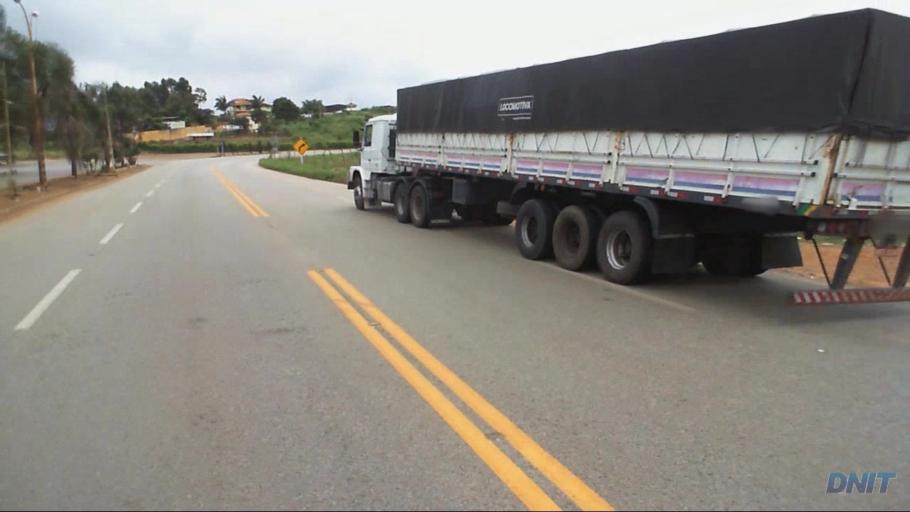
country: BR
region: Minas Gerais
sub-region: Nova Era
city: Nova Era
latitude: -19.8089
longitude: -43.0639
